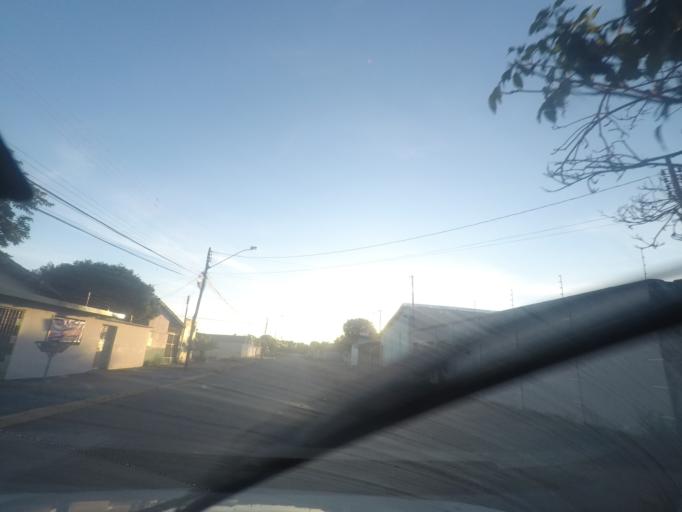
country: BR
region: Goias
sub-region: Goiania
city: Goiania
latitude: -16.6878
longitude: -49.3544
